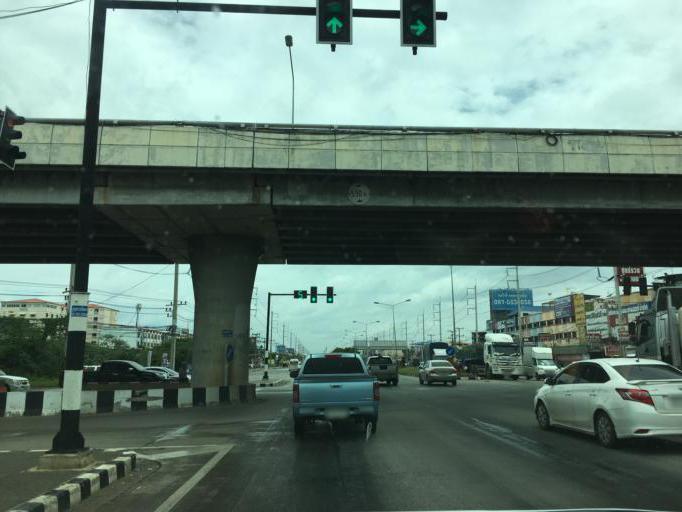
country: TH
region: Phra Nakhon Si Ayutthaya
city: Uthai
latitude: 14.3106
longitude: 100.6431
